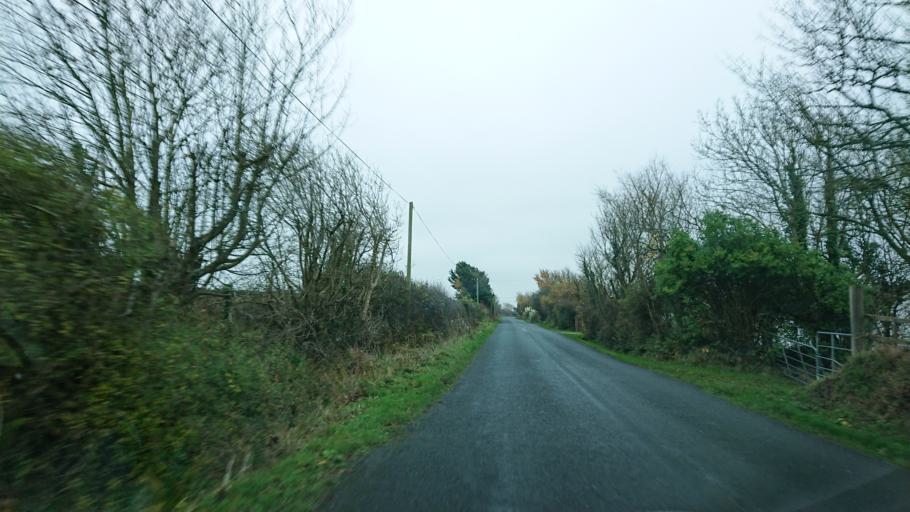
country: IE
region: Munster
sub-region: Waterford
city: Tra Mhor
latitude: 52.1689
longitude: -7.0687
